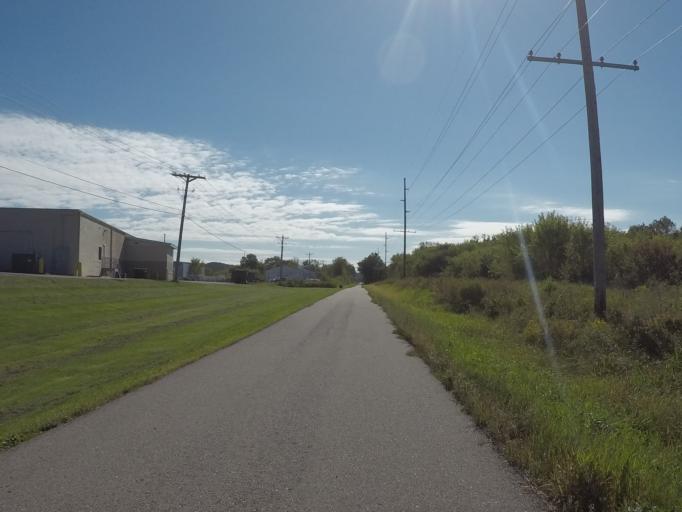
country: US
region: Wisconsin
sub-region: Richland County
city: Richland Center
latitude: 43.3167
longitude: -90.3616
